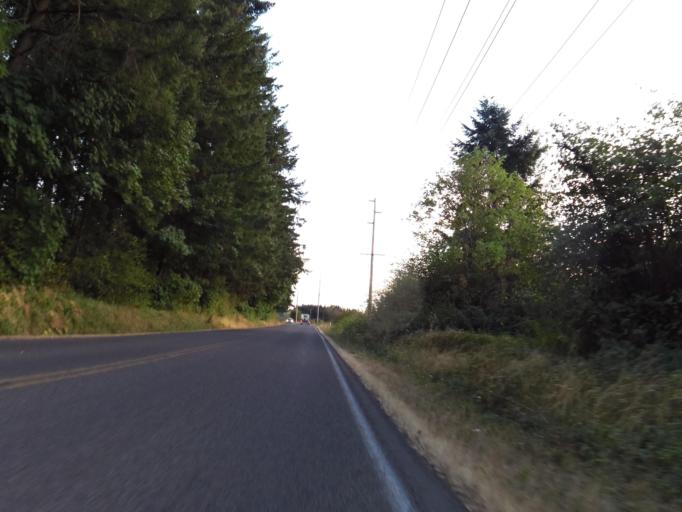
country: US
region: Washington
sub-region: Thurston County
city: Tenino
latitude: 46.8477
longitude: -122.8600
